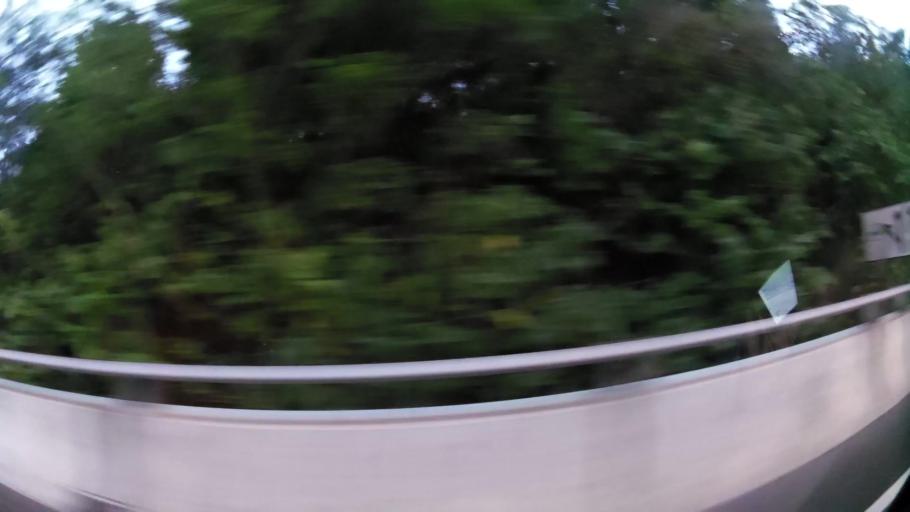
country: HK
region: Tsuen Wan
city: Tsuen Wan
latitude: 22.3603
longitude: 114.0941
